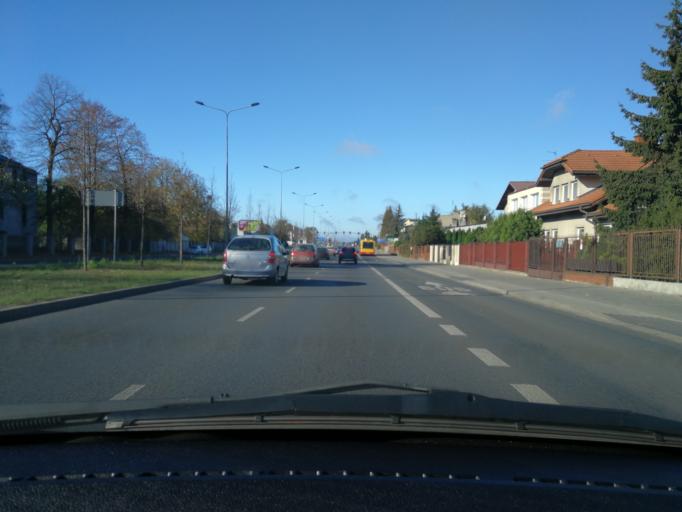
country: PL
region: Lodz Voivodeship
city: Lodz
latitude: 51.8003
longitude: 19.4756
